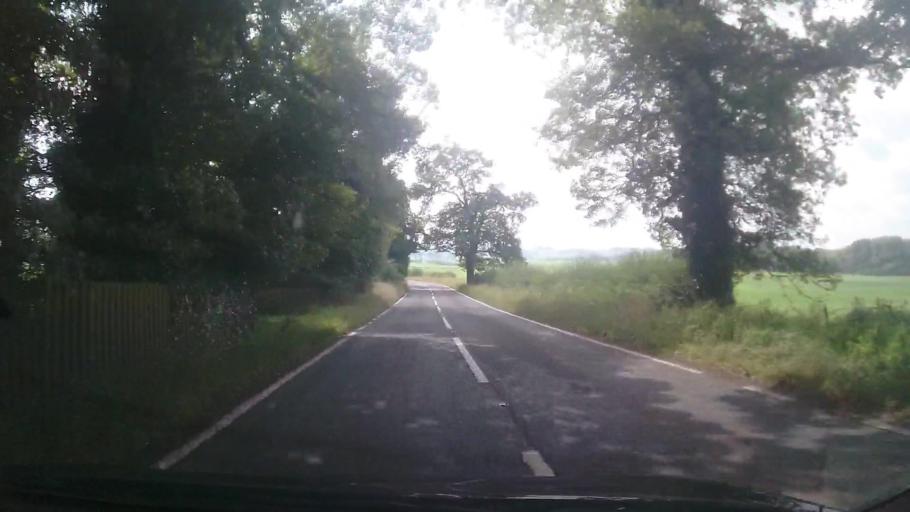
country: GB
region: England
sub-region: Cheshire West and Chester
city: Bickley
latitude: 53.0244
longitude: -2.6853
